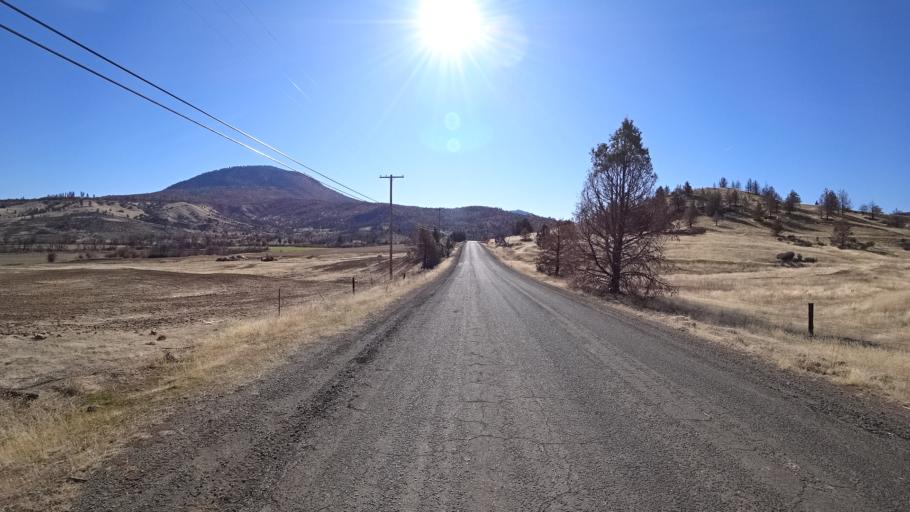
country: US
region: California
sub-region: Siskiyou County
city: Montague
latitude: 41.8935
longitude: -122.5502
